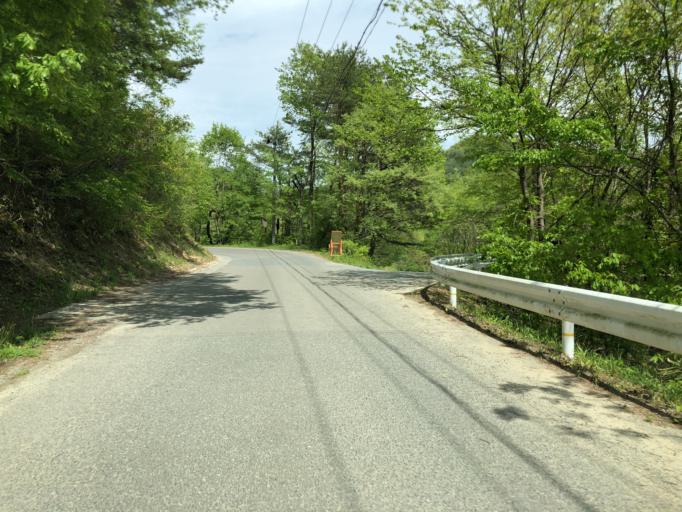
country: JP
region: Fukushima
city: Yanagawamachi-saiwaicho
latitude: 37.7395
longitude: 140.7065
